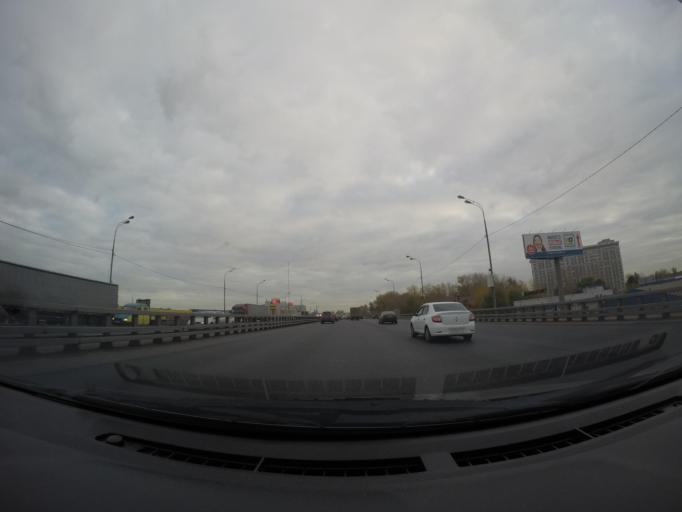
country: RU
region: Moskovskaya
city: Reutov
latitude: 55.7813
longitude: 37.8620
